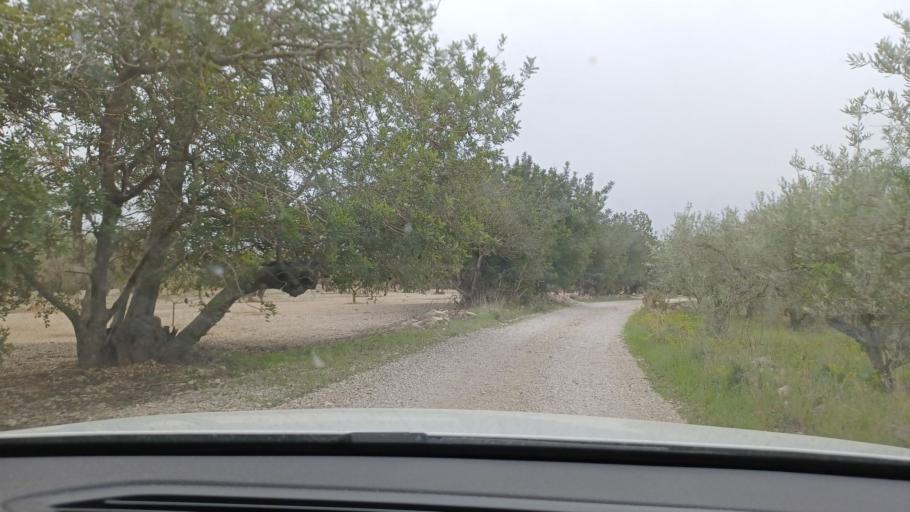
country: ES
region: Catalonia
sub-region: Provincia de Tarragona
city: Mas de Barberans
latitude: 40.8035
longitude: 0.4131
